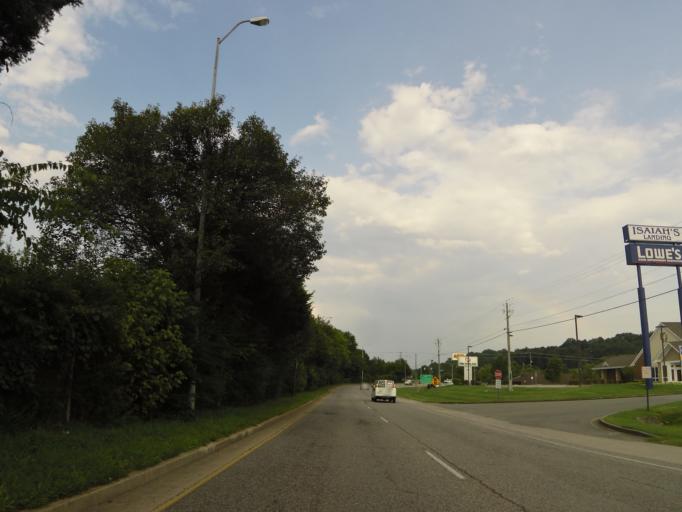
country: US
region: Tennessee
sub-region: Knox County
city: Knoxville
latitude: 36.0296
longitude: -83.8755
